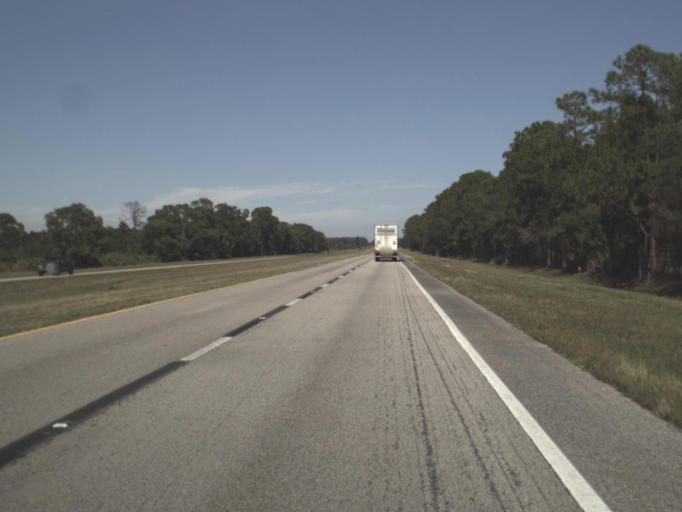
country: US
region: Florida
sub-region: Highlands County
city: Placid Lakes
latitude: 27.0369
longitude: -81.3420
